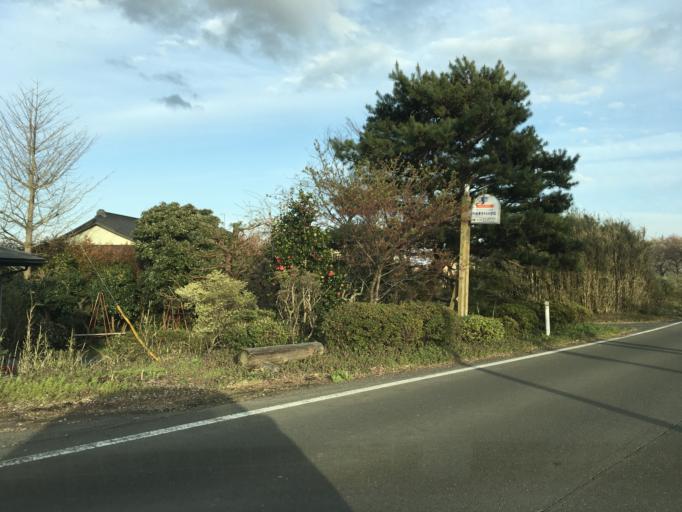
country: JP
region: Miyagi
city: Wakuya
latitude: 38.6465
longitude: 141.1459
